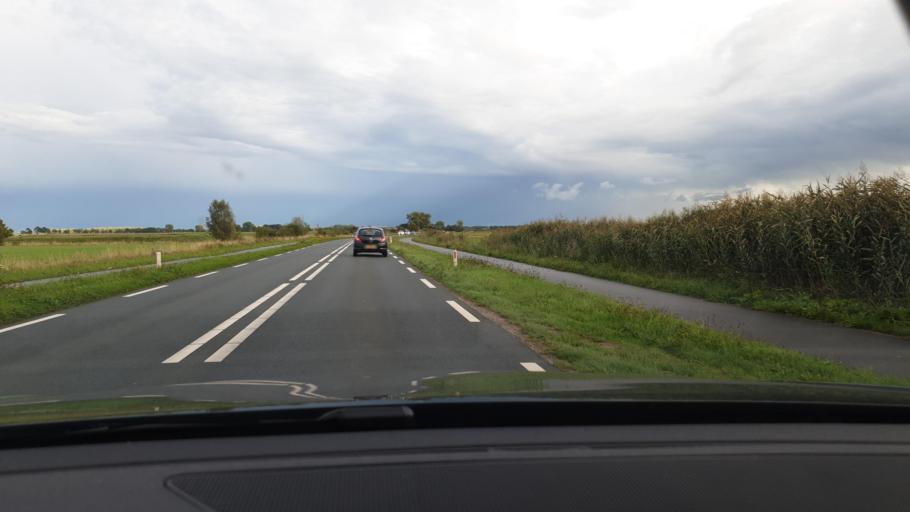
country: NL
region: North Brabant
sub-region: Gemeente Oss
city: Berghem
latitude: 51.8047
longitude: 5.5915
